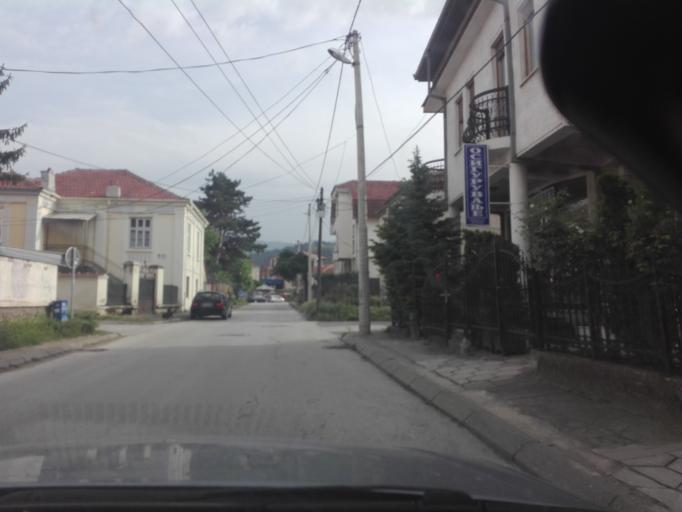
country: MK
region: Bitola
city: Bitola
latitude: 41.0259
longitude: 21.3402
